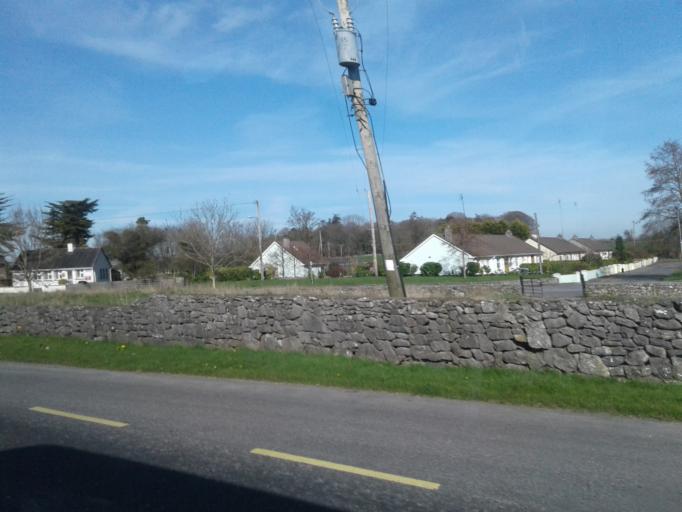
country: IE
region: Connaught
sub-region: County Galway
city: Gort
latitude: 53.1547
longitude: -8.8054
